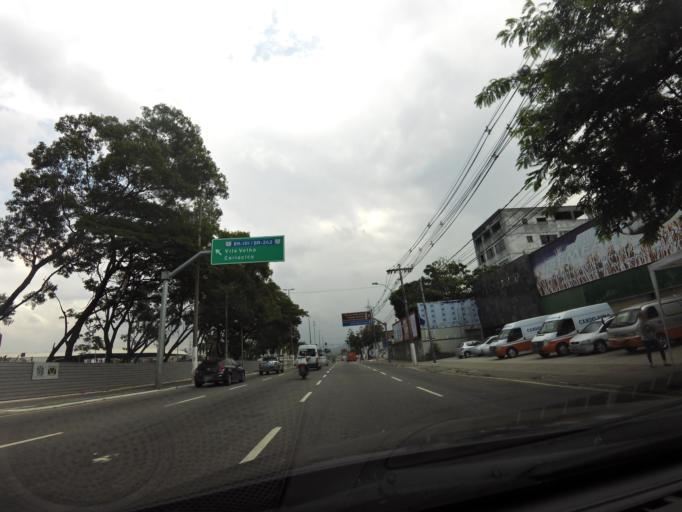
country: BR
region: Espirito Santo
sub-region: Vitoria
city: Vitoria
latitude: -20.3196
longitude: -40.3501
